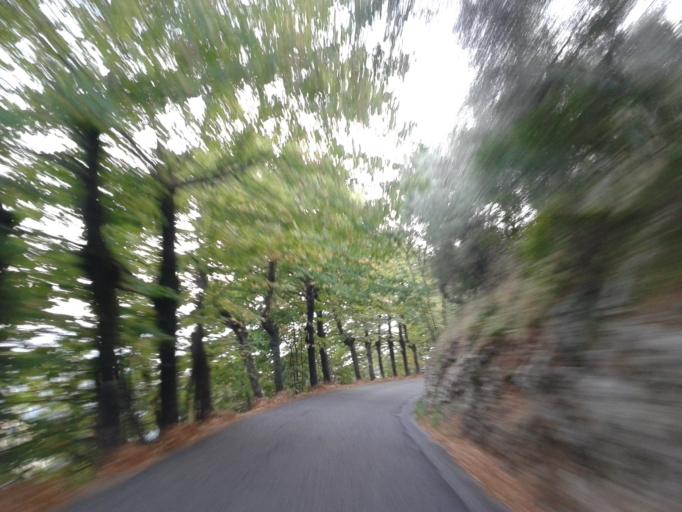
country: IT
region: Tuscany
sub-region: Provincia di Lucca
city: Pontestazzemese
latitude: 43.9558
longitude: 10.3184
